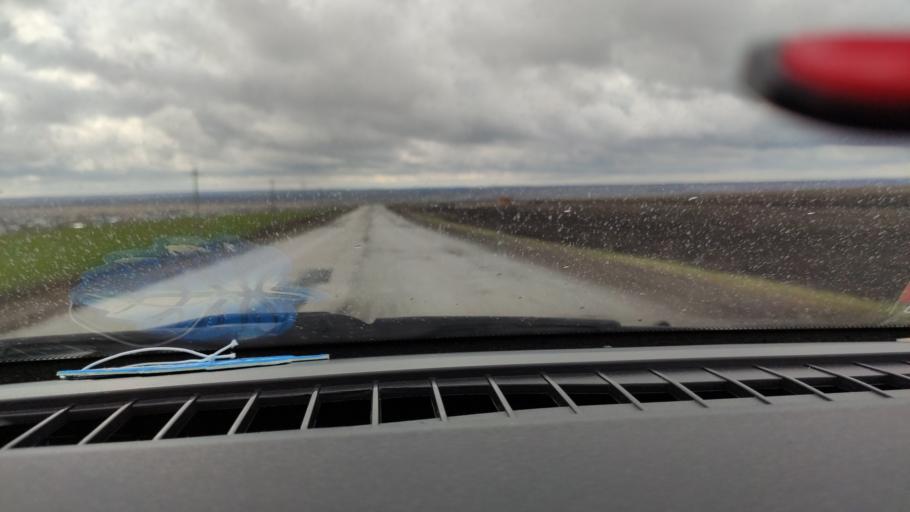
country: RU
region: Tatarstan
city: Nurlat
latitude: 54.4033
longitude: 50.7821
